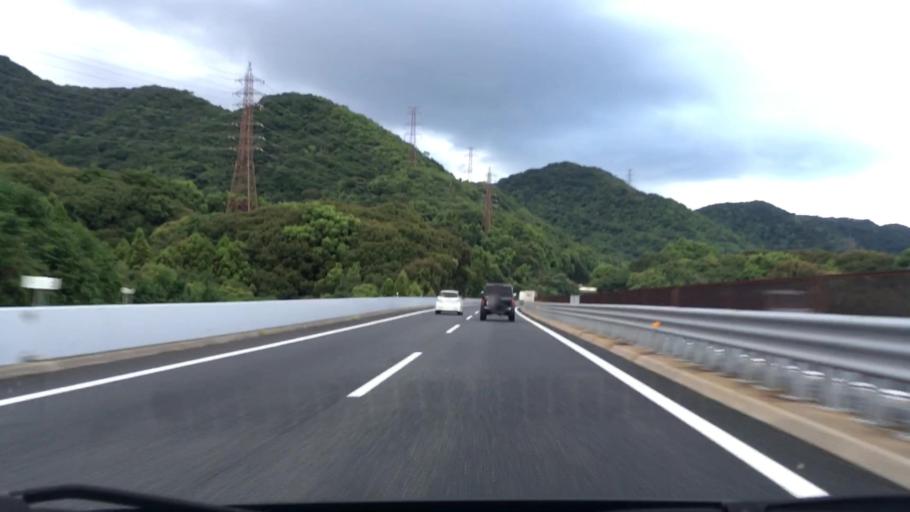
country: JP
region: Fukuoka
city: Kanda
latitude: 33.8575
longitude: 130.9390
